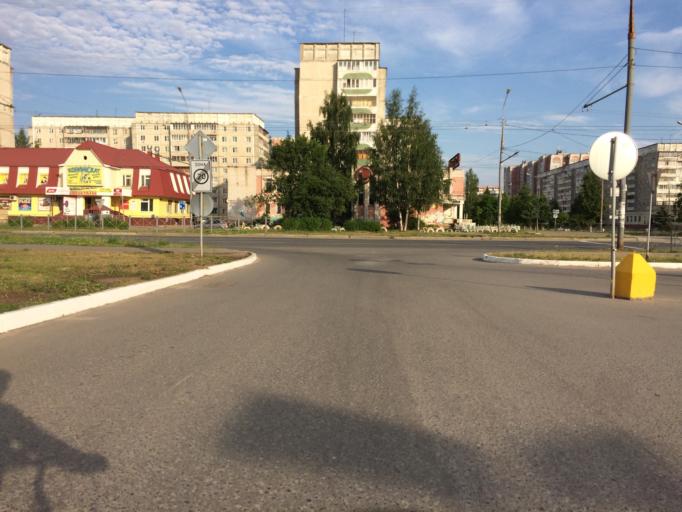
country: RU
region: Mariy-El
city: Yoshkar-Ola
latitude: 56.6280
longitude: 47.9280
